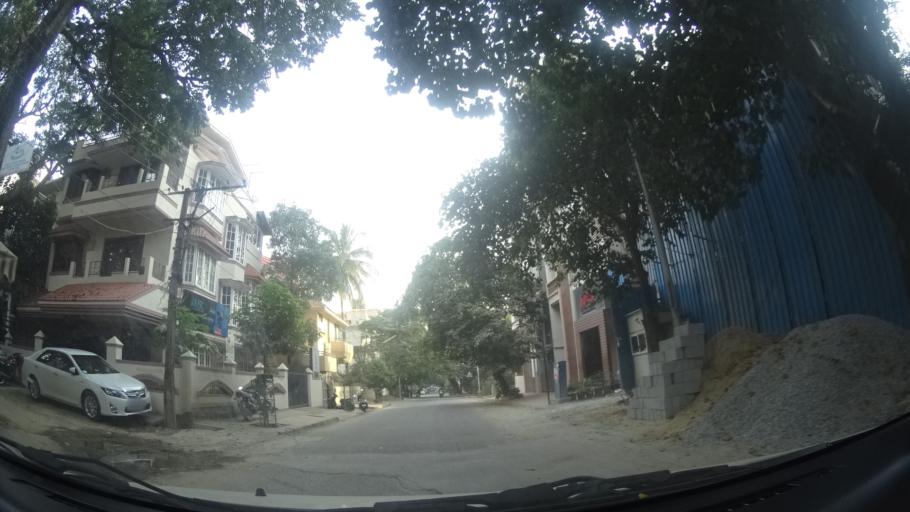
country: IN
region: Karnataka
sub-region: Bangalore Urban
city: Bangalore
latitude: 13.0008
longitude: 77.6246
